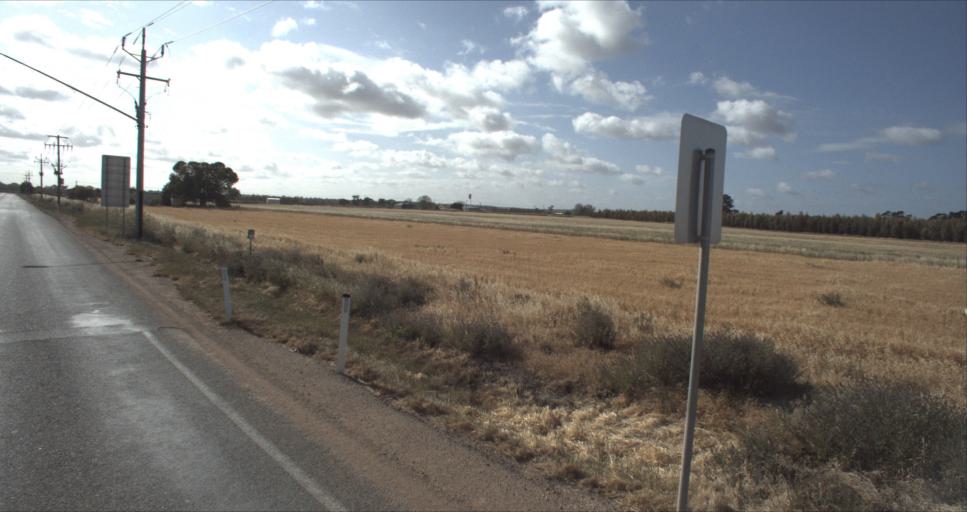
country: AU
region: New South Wales
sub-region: Leeton
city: Leeton
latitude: -34.5715
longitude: 146.3953
